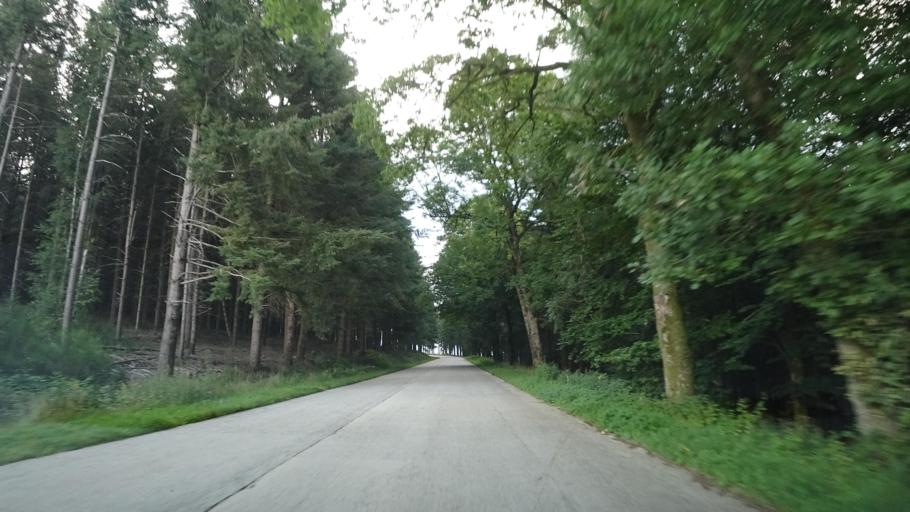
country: BE
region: Wallonia
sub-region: Province du Luxembourg
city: Herbeumont
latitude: 49.7922
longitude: 5.2549
